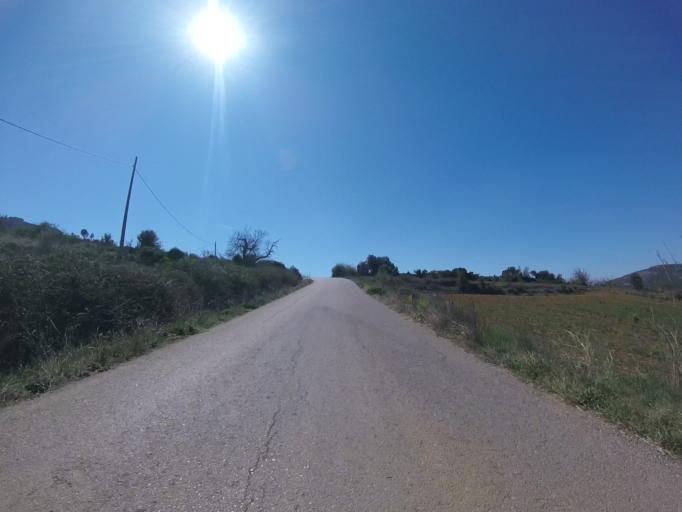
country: ES
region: Valencia
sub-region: Provincia de Castello
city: Chert/Xert
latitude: 40.4110
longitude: 0.1745
